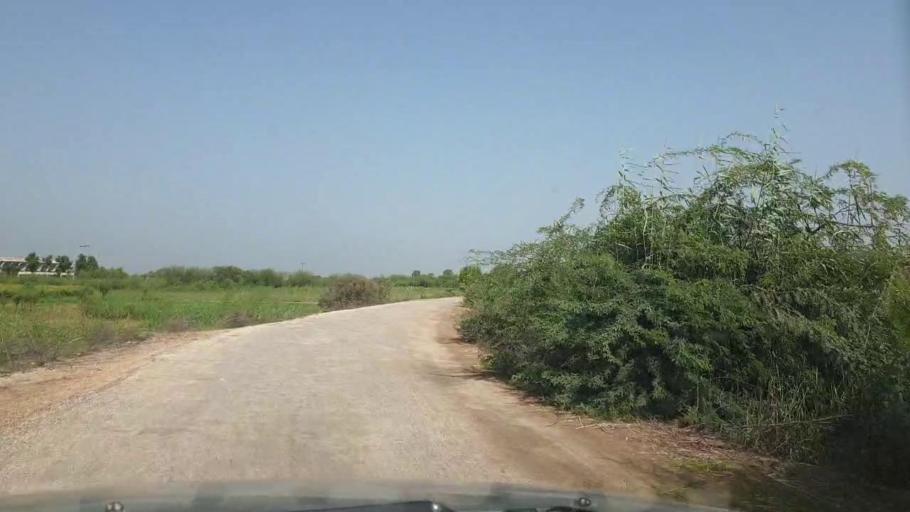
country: PK
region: Sindh
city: Tando Ghulam Ali
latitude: 25.0991
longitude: 68.7654
